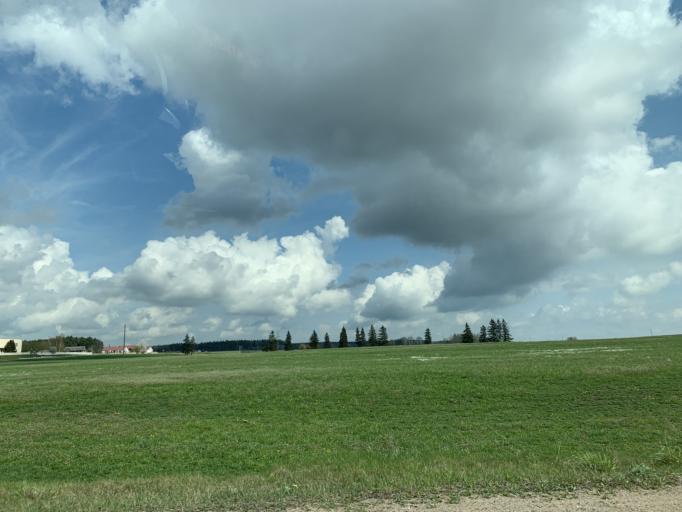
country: BY
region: Minsk
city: Nyasvizh
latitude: 53.2505
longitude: 26.6900
